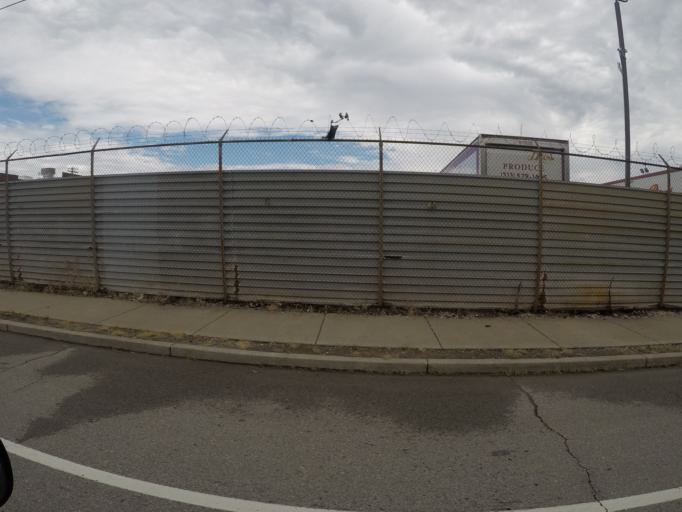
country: US
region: Michigan
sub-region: Wayne County
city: Hamtramck
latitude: 42.3721
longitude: -83.0235
